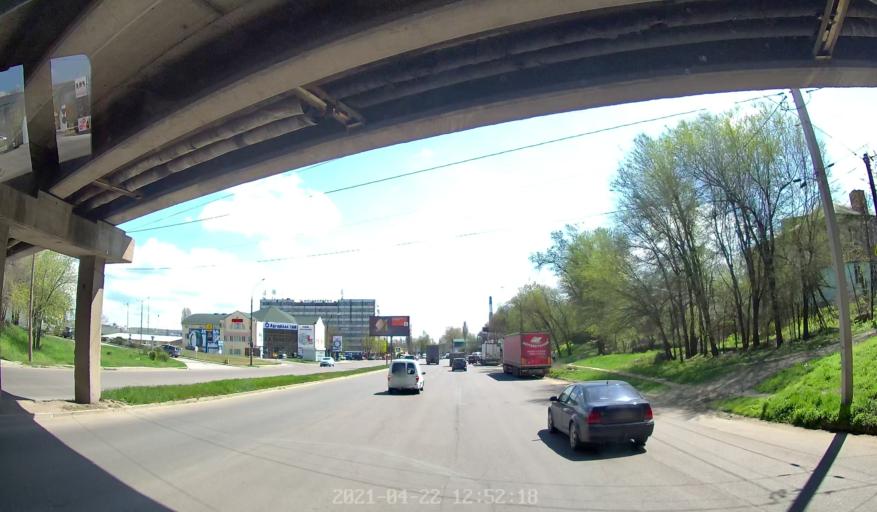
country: NG
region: Niger
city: Lemu
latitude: 9.3961
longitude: 5.7801
